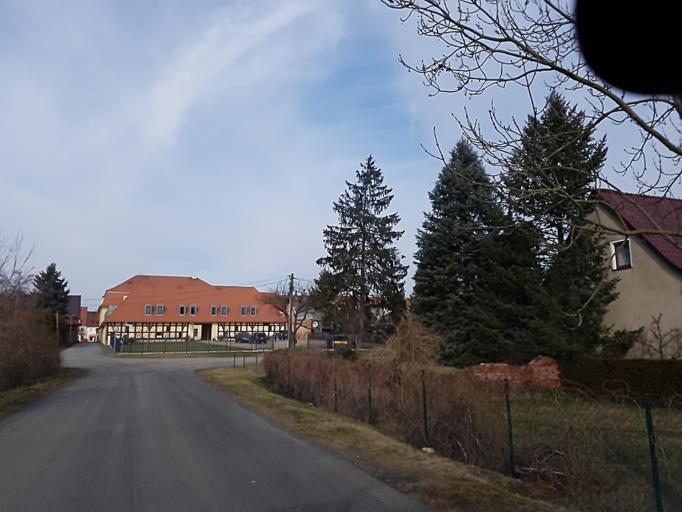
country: DE
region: Brandenburg
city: Doberlug-Kirchhain
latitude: 51.6096
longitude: 13.5509
